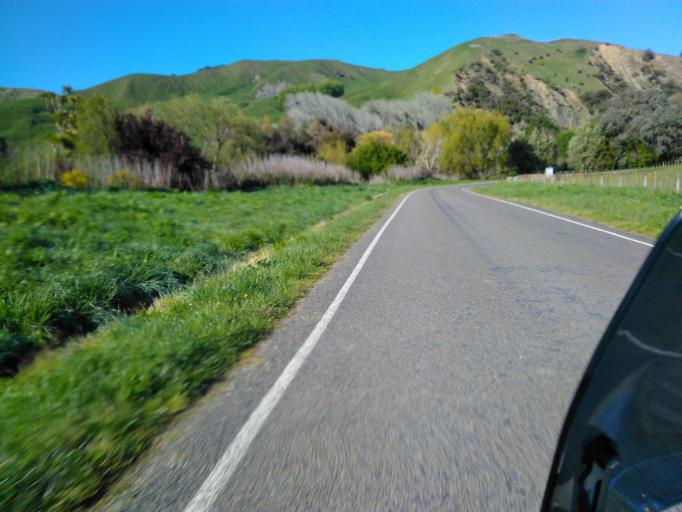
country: NZ
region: Gisborne
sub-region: Gisborne District
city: Gisborne
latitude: -38.4277
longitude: 177.7305
